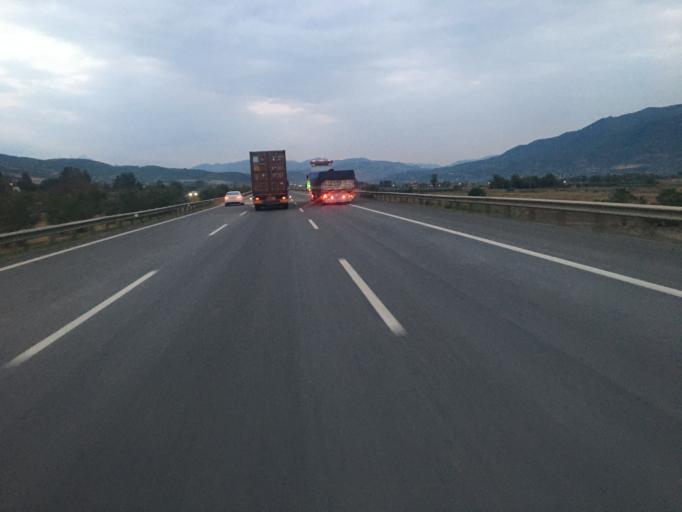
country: TR
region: Osmaniye
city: Osmaniye
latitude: 37.1320
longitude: 36.3068
